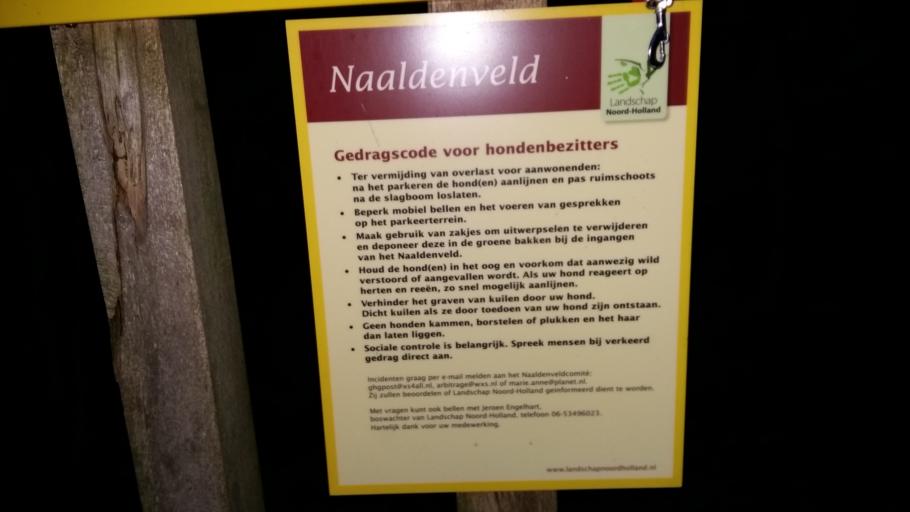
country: NL
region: North Holland
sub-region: Gemeente Bloemendaal
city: Bennebroek
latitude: 52.3597
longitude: 4.5777
